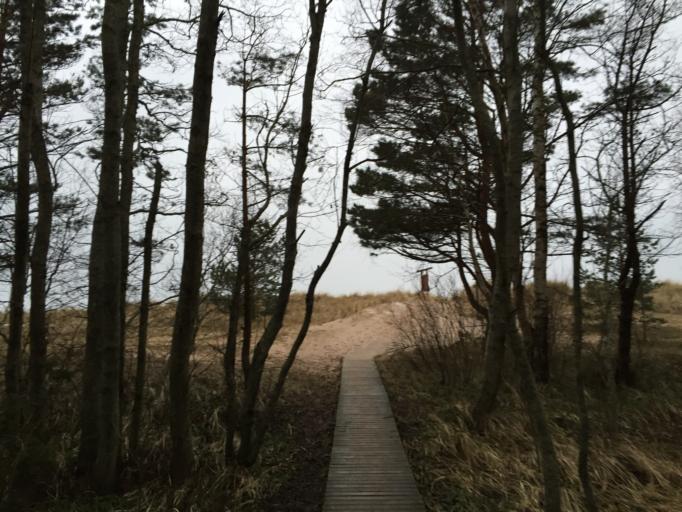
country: EE
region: Saare
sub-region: Kuressaare linn
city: Kuressaare
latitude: 58.5925
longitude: 22.5025
